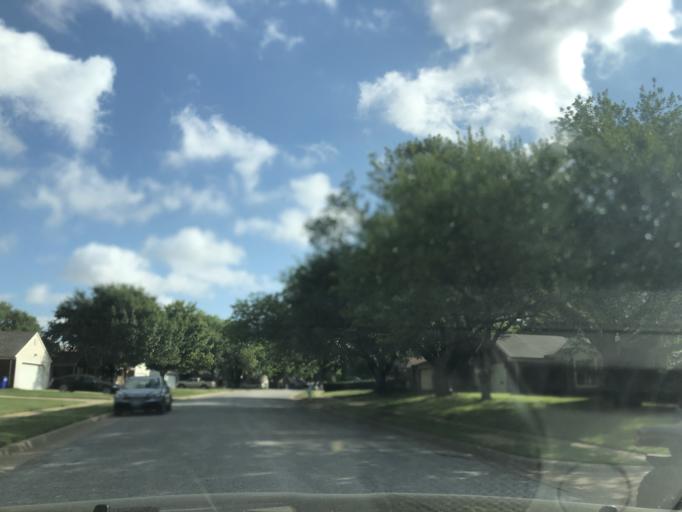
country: US
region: Texas
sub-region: Tarrant County
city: Euless
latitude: 32.8749
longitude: -97.0782
